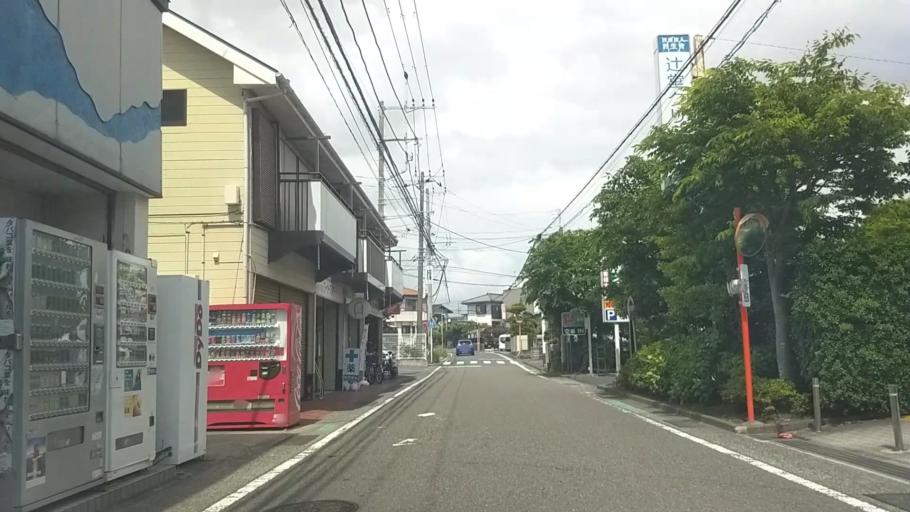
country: JP
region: Kanagawa
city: Fujisawa
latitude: 35.3426
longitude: 139.4540
